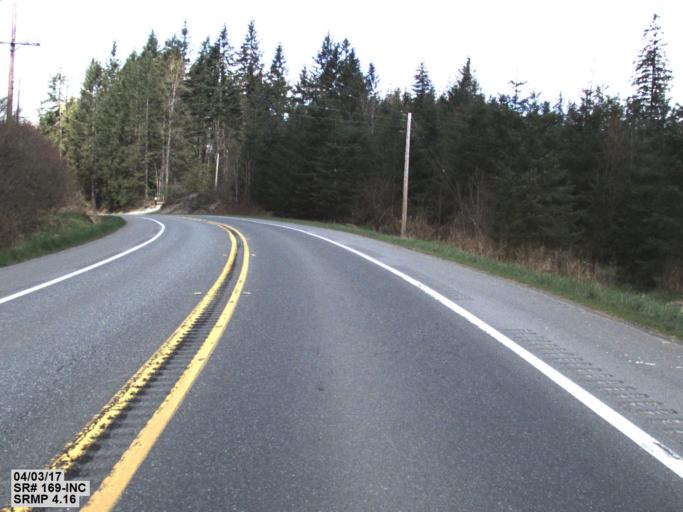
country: US
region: Washington
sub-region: King County
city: Black Diamond
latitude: 47.2637
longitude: -121.9858
